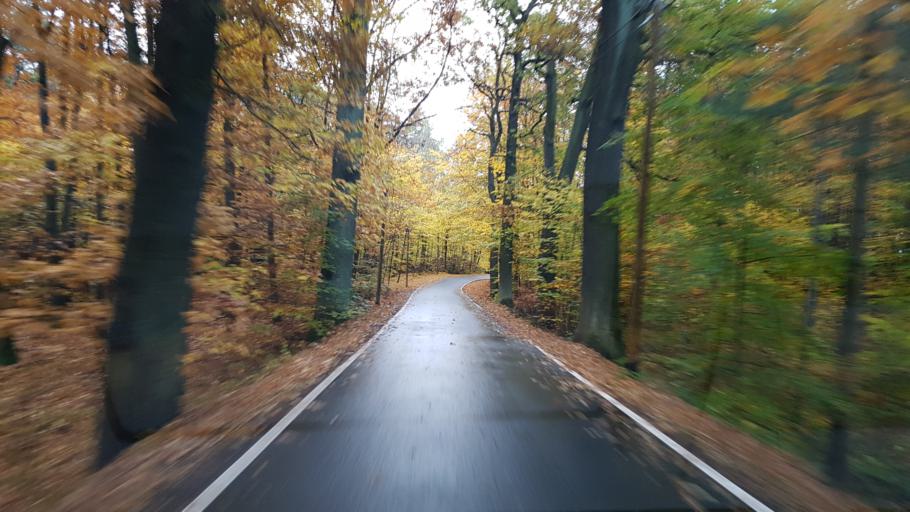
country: DE
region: Saxony
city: Cavertitz
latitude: 51.3951
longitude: 13.0640
